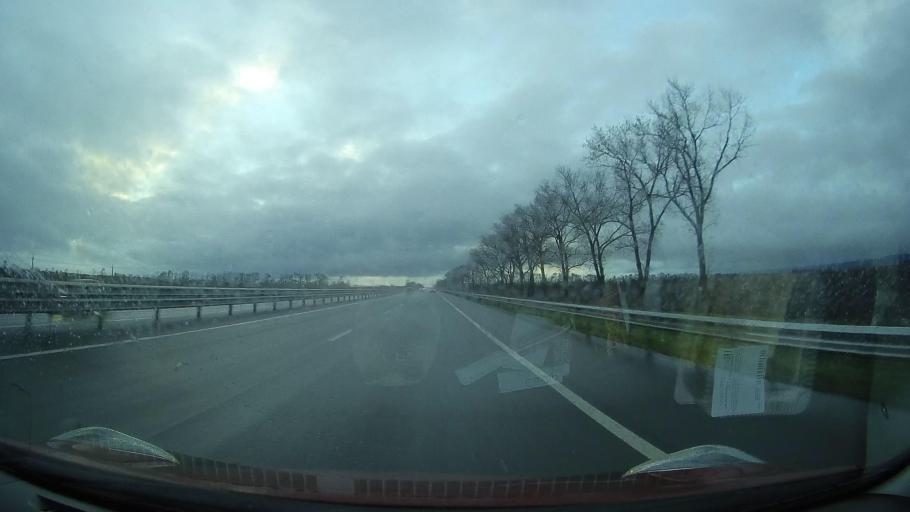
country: RU
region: Stavropol'skiy
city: Zavetnoye
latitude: 44.7885
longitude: 41.5057
